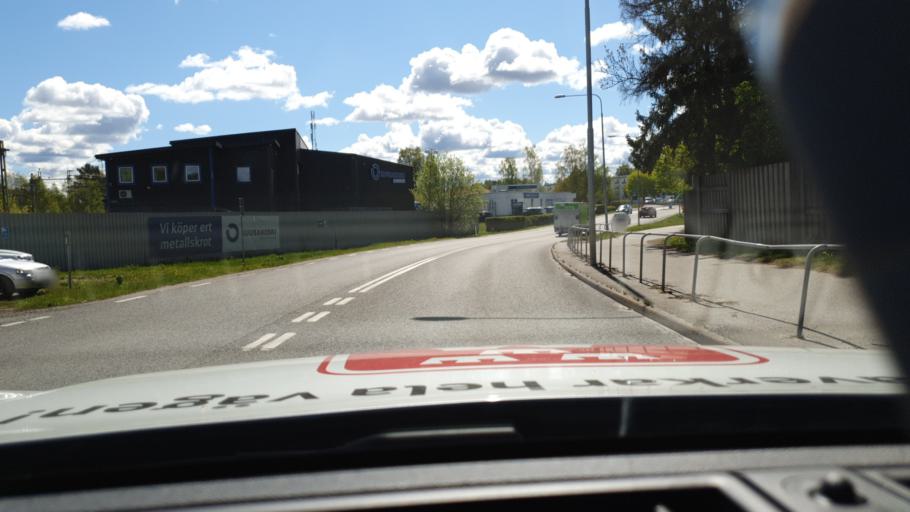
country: SE
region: Stockholm
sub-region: Stockholms Kommun
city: Kista
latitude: 59.3805
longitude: 17.9038
